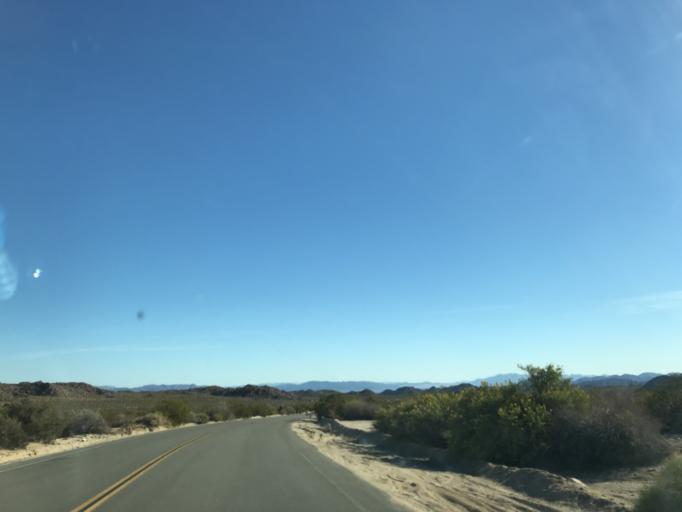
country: US
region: California
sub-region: Riverside County
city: Mecca
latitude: 33.7932
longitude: -115.7899
